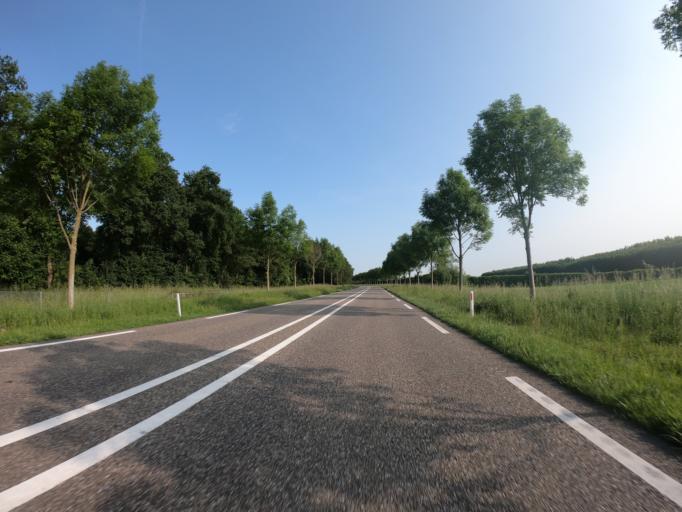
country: NL
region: North Brabant
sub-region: Gemeente Landerd
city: Reek
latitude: 51.7823
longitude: 5.6651
